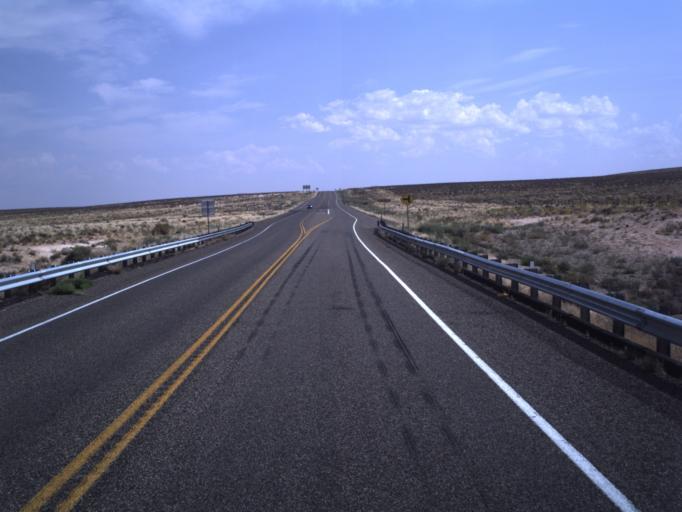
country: US
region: Arizona
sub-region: Coconino County
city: Page
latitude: 37.0079
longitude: -111.5798
